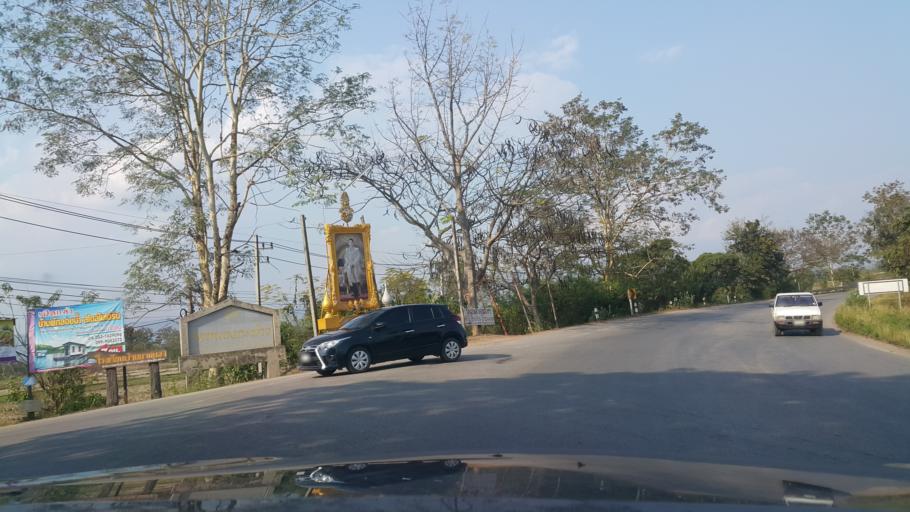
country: TH
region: Phitsanulok
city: Nakhon Thai
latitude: 17.0688
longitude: 100.8089
